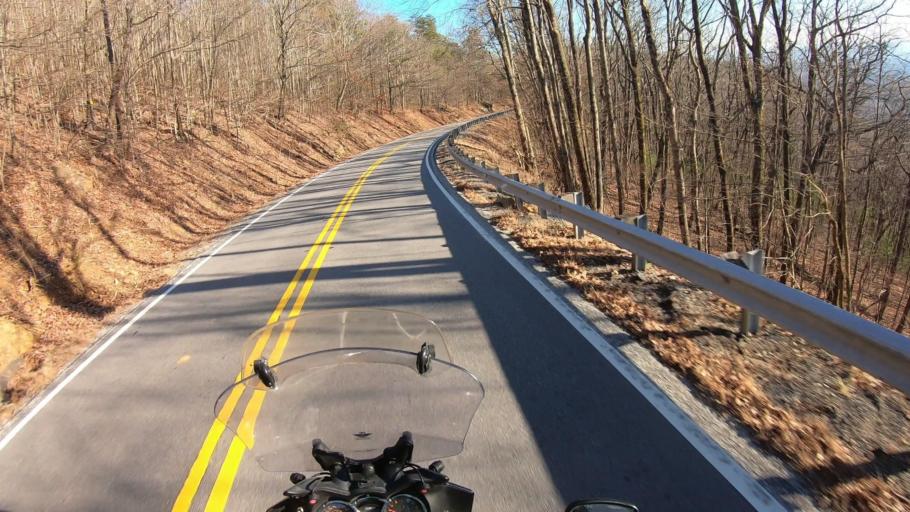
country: US
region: Georgia
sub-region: Lumpkin County
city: Dahlonega
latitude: 34.6707
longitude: -83.9919
